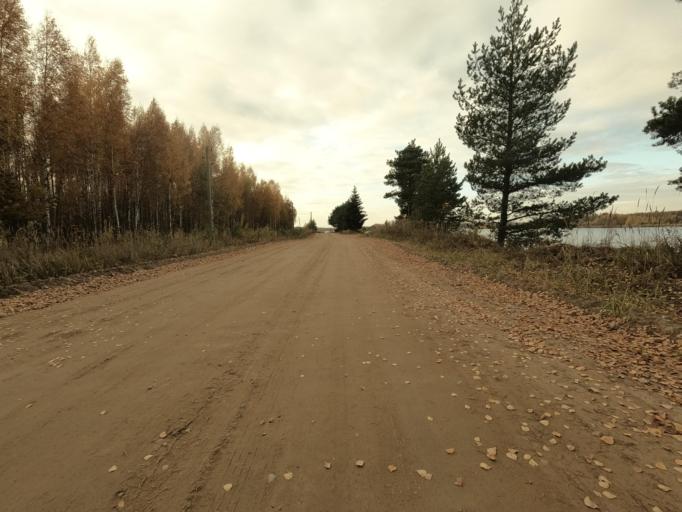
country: RU
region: Leningrad
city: Priladozhskiy
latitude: 59.7129
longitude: 31.3516
